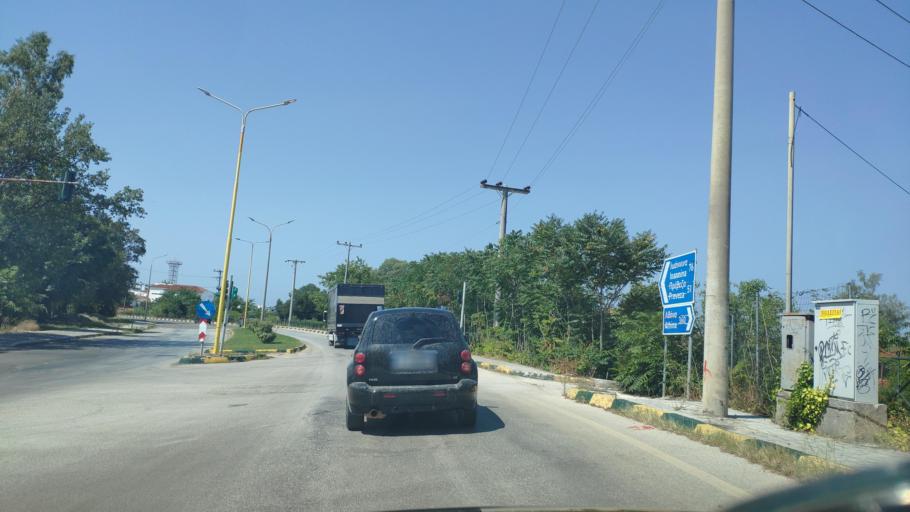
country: GR
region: Epirus
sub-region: Nomos Artas
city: Arta
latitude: 39.1652
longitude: 20.9825
